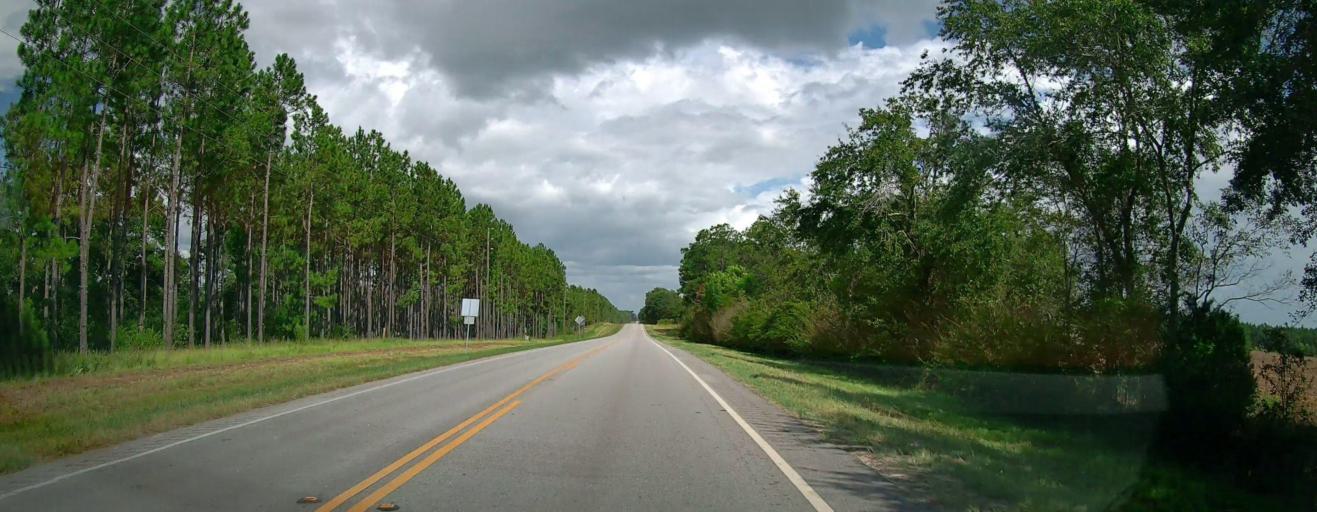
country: US
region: Georgia
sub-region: Coffee County
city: Broxton
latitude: 31.5787
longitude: -83.0553
